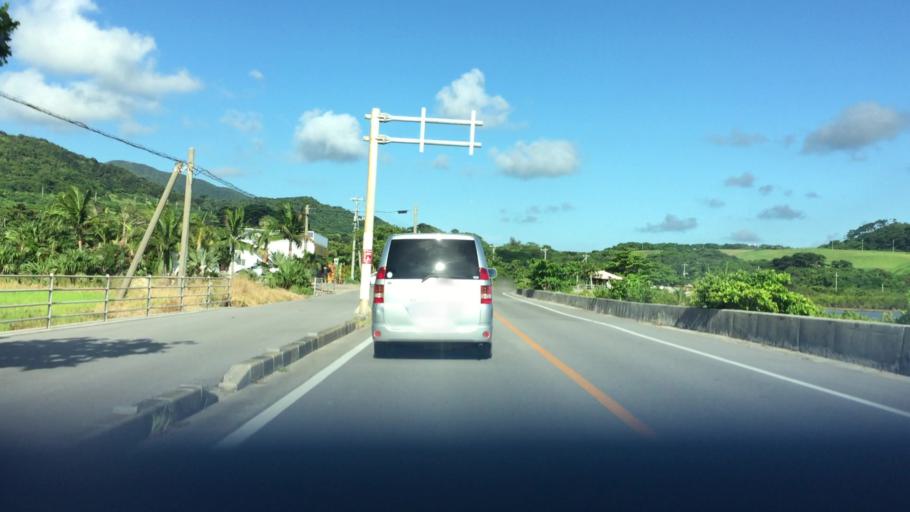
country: JP
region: Okinawa
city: Ishigaki
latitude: 24.4148
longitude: 124.1404
